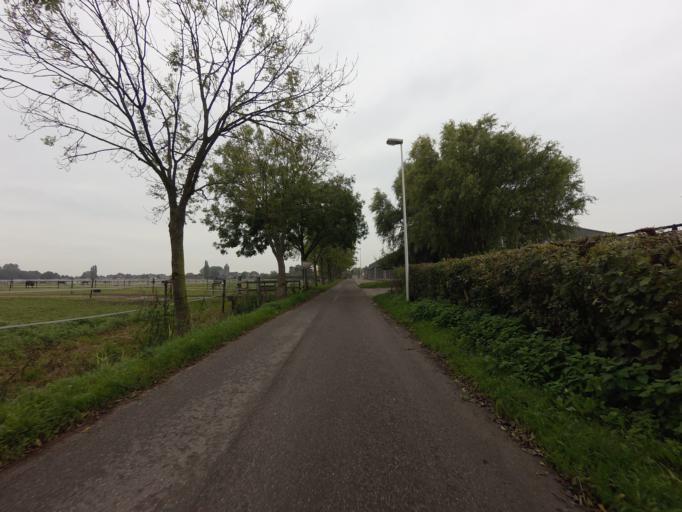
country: NL
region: Utrecht
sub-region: Gemeente Vianen
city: Vianen
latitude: 51.9833
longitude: 5.1151
